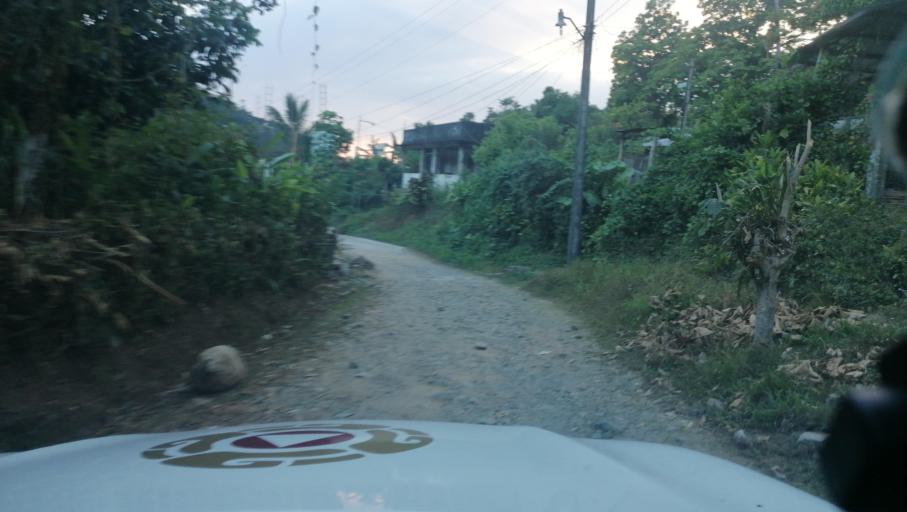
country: MX
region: Chiapas
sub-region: Cacahoatan
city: Benito Juarez
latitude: 15.0739
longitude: -92.2271
